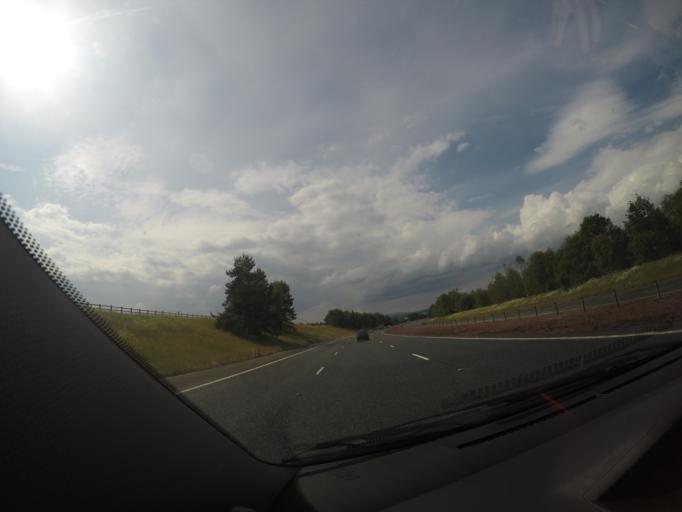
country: GB
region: Scotland
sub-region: Dumfries and Galloway
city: Lochmaben
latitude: 55.1754
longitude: -3.4006
